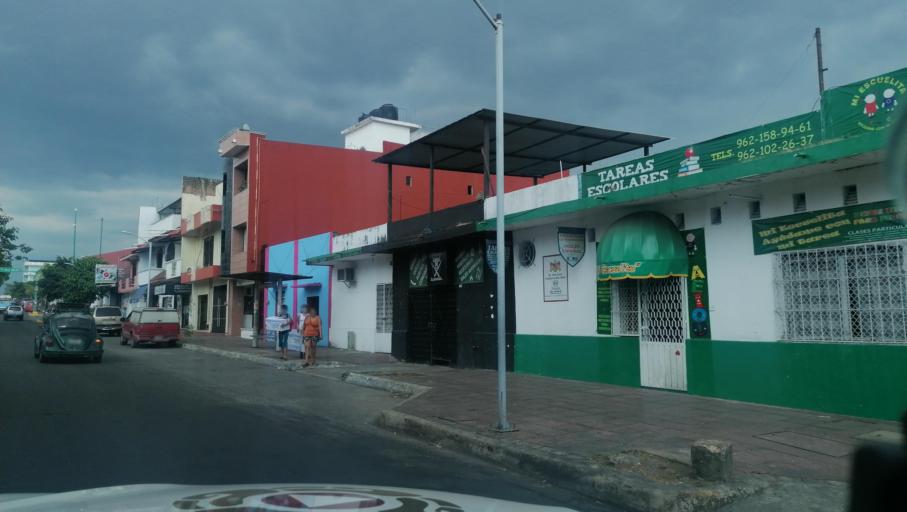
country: MX
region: Chiapas
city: Tapachula
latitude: 14.9076
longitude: -92.2566
